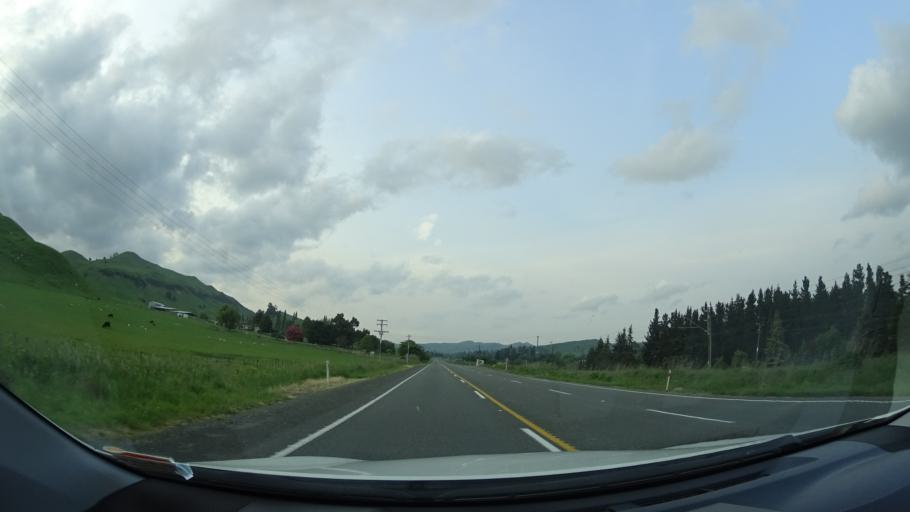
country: NZ
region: Manawatu-Wanganui
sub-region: Ruapehu District
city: Waiouru
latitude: -39.7252
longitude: 175.8423
